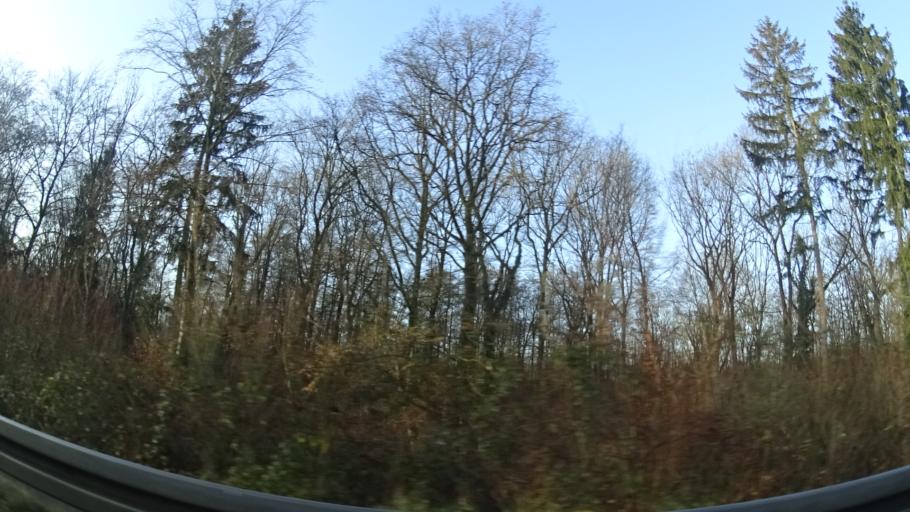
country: DE
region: Baden-Wuerttemberg
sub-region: Karlsruhe Region
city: Hambrucken
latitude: 49.1697
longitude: 8.5514
